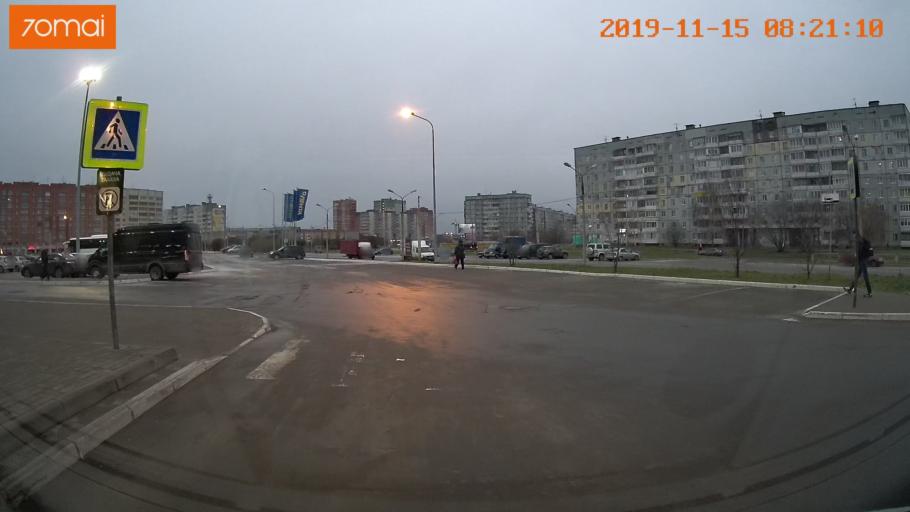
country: RU
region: Vologda
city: Cherepovets
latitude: 59.0932
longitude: 37.9178
